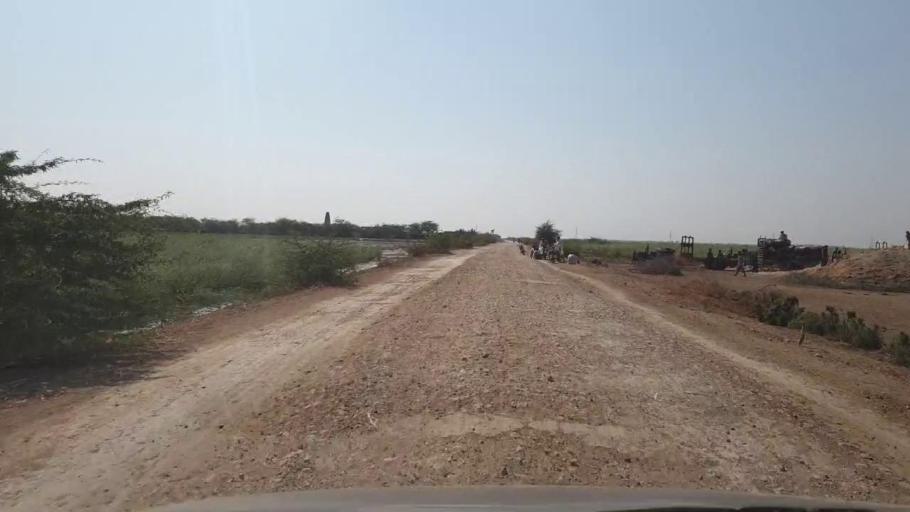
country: PK
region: Sindh
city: Digri
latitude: 25.2066
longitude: 69.2311
